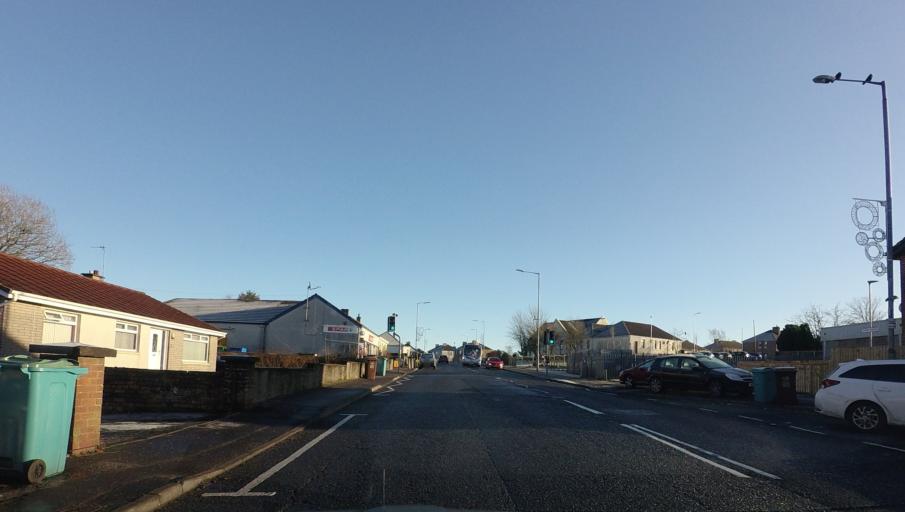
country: GB
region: Scotland
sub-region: North Lanarkshire
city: Shotts
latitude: 55.8003
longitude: -3.8364
